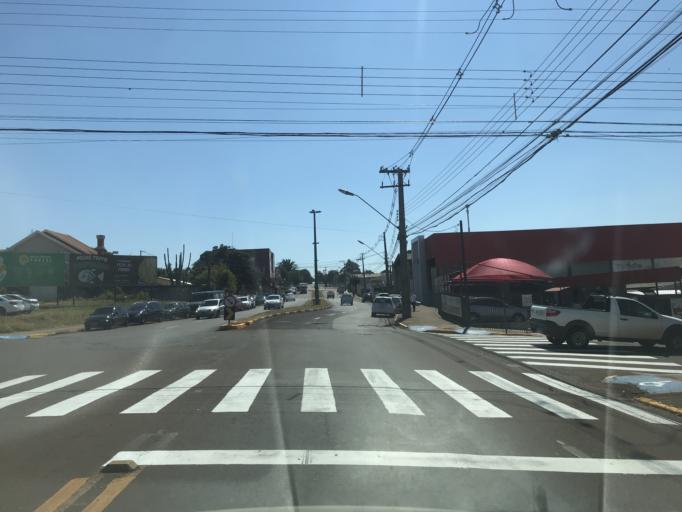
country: BR
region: Parana
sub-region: Toledo
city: Toledo
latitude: -24.7292
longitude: -53.7361
